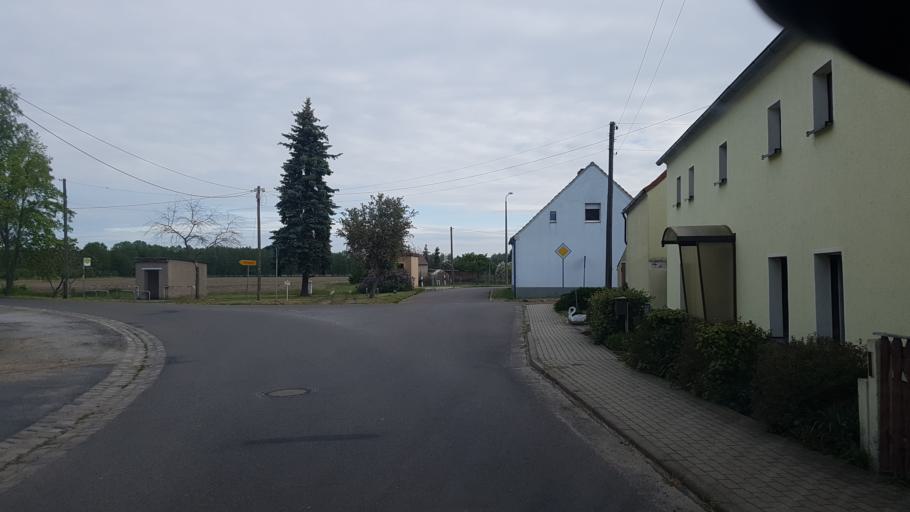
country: DE
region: Brandenburg
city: Luckenwalde
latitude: 52.1129
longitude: 13.1112
